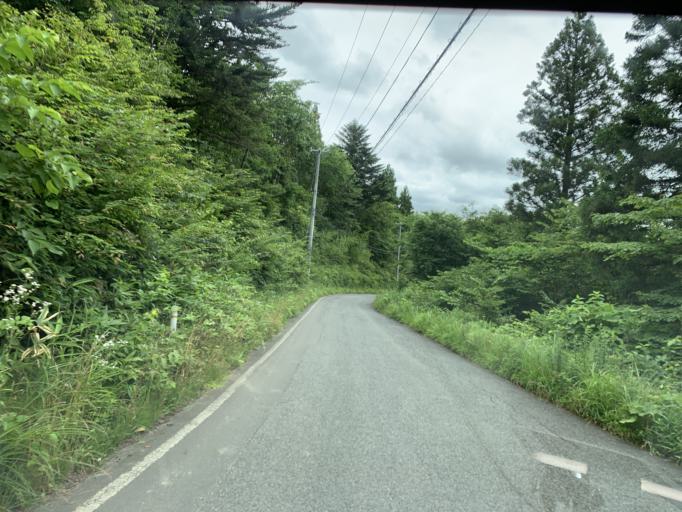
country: JP
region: Iwate
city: Ichinoseki
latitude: 38.9098
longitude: 141.0218
